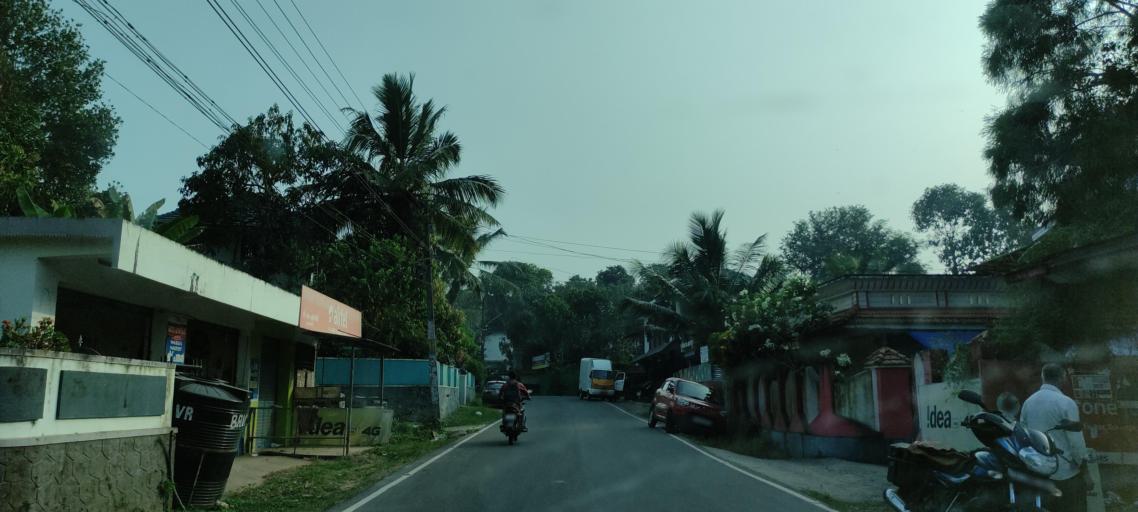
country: IN
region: Kerala
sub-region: Pattanamtitta
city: Adur
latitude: 9.1174
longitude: 76.7315
